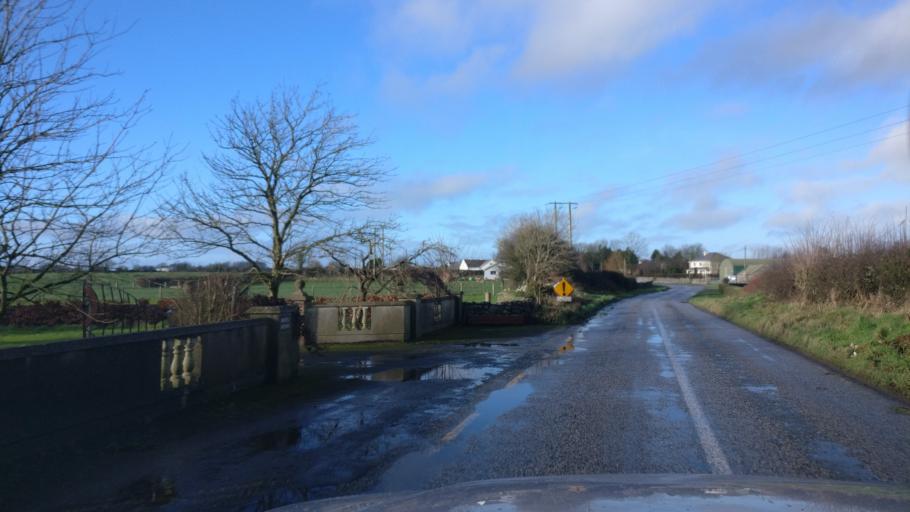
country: IE
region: Connaught
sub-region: County Galway
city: Athenry
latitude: 53.2618
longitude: -8.6832
